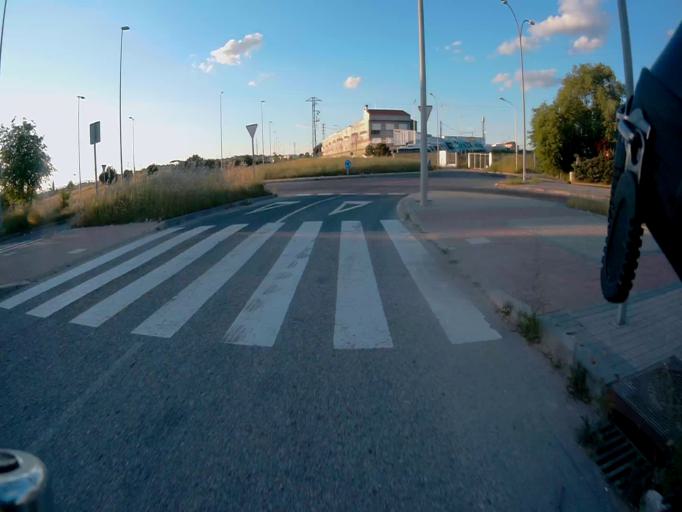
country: ES
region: Madrid
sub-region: Provincia de Madrid
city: Alcorcon
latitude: 40.3293
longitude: -3.8185
